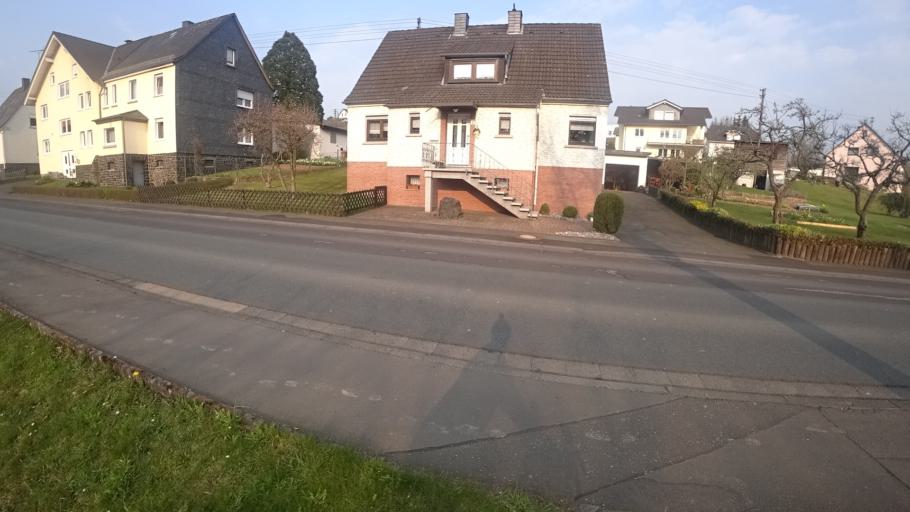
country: DE
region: Rheinland-Pfalz
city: Luckenbach
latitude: 50.7000
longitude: 7.8331
